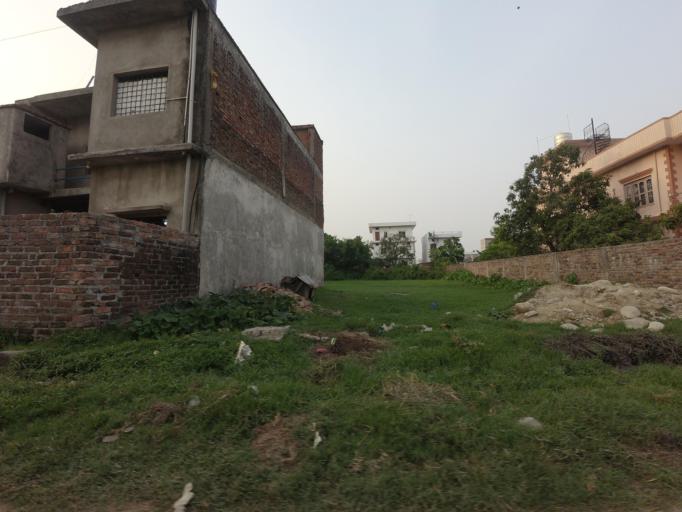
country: NP
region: Western Region
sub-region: Lumbini Zone
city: Bhairahawa
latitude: 27.5180
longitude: 83.4562
